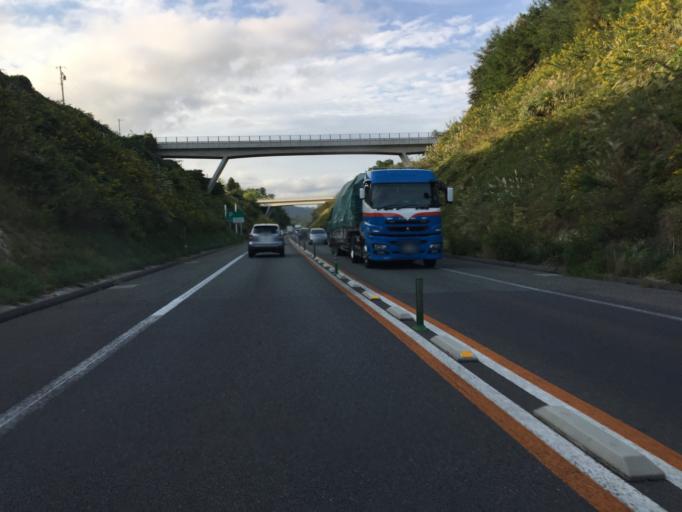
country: JP
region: Fukushima
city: Namie
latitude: 37.2672
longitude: 140.9866
